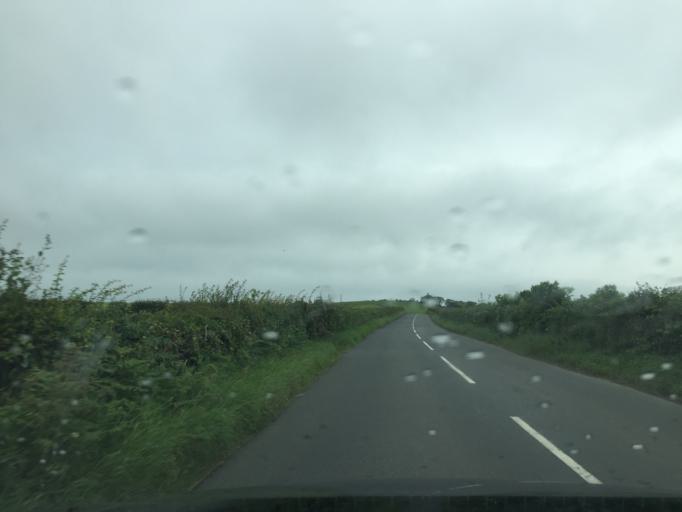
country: GB
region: Northern Ireland
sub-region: Down District
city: Kircubbin
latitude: 54.4929
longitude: -5.5070
